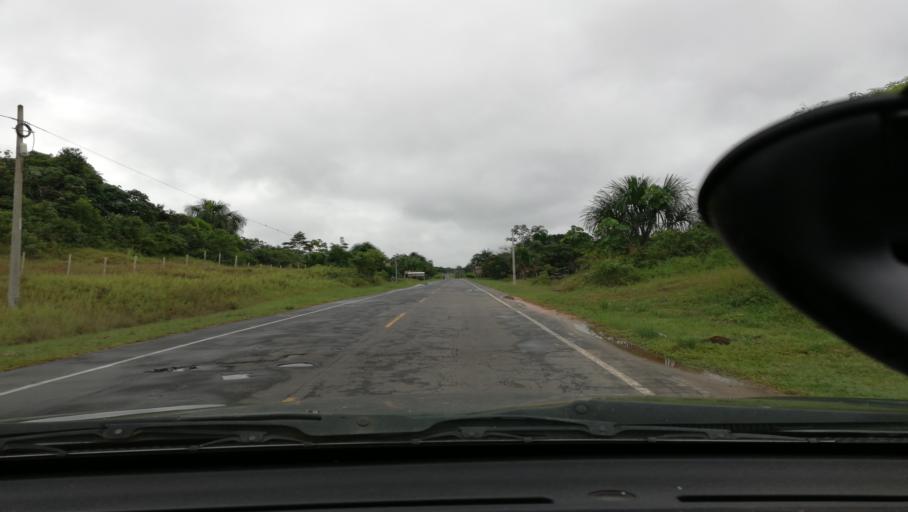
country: PE
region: Loreto
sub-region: Provincia de Loreto
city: Nauta
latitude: -4.3422
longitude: -73.5392
